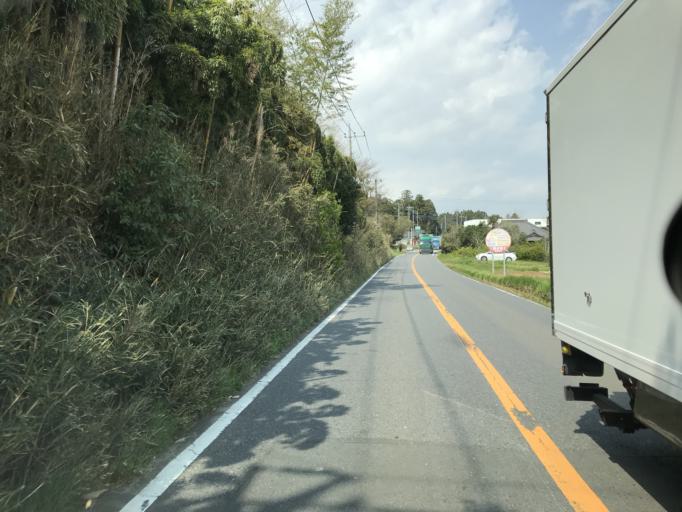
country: JP
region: Chiba
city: Sawara
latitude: 35.8631
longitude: 140.5471
